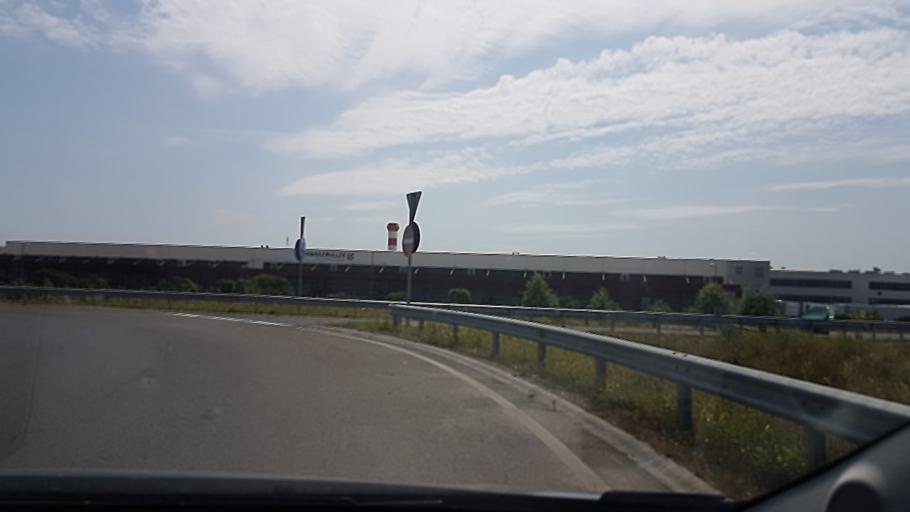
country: HU
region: Pest
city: Dunaharaszti
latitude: 47.3670
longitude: 19.1156
